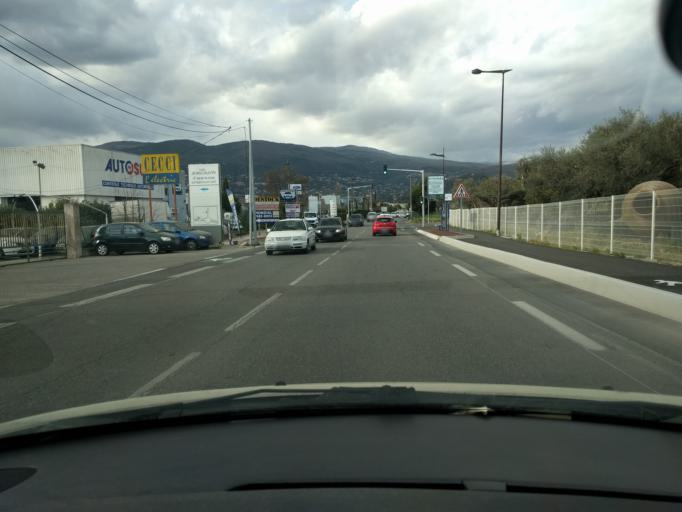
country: FR
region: Provence-Alpes-Cote d'Azur
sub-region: Departement des Alpes-Maritimes
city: Mouans-Sartoux
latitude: 43.6356
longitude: 6.9568
